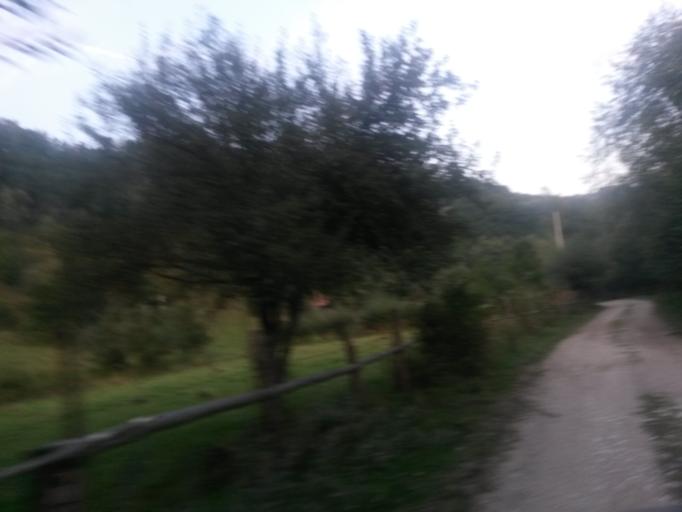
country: RO
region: Alba
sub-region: Comuna Ponor
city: Ponor
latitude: 46.3106
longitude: 23.4071
